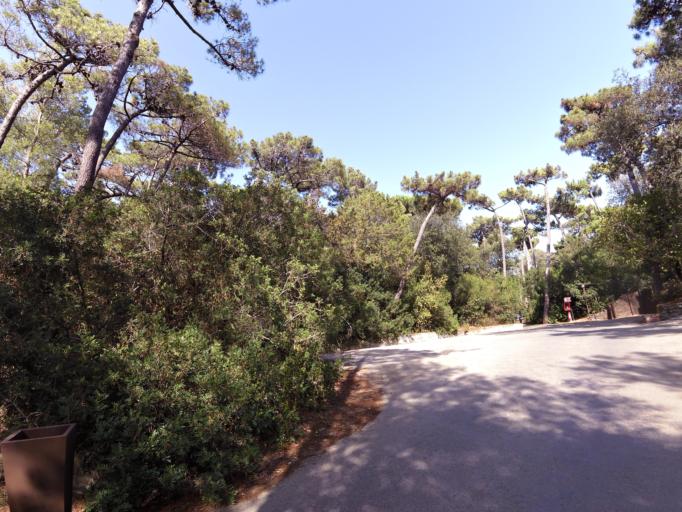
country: IT
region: Tuscany
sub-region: Provincia di Livorno
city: Donoratico
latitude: 43.1539
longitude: 10.5417
